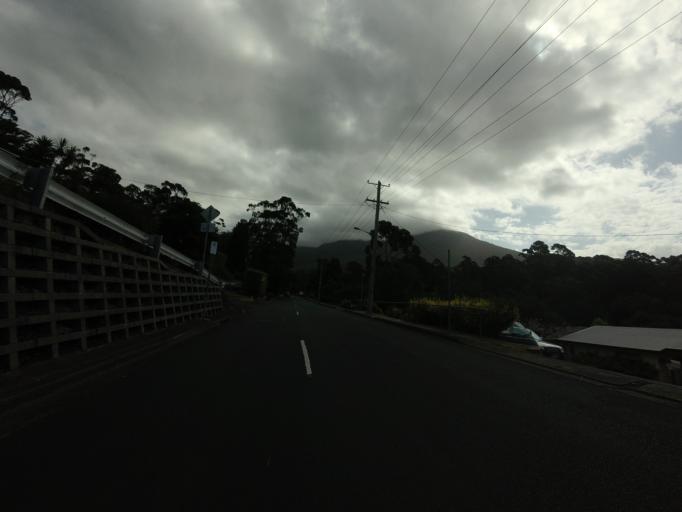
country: AU
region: Tasmania
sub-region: Hobart
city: Dynnyrne
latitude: -42.8985
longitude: 147.2851
